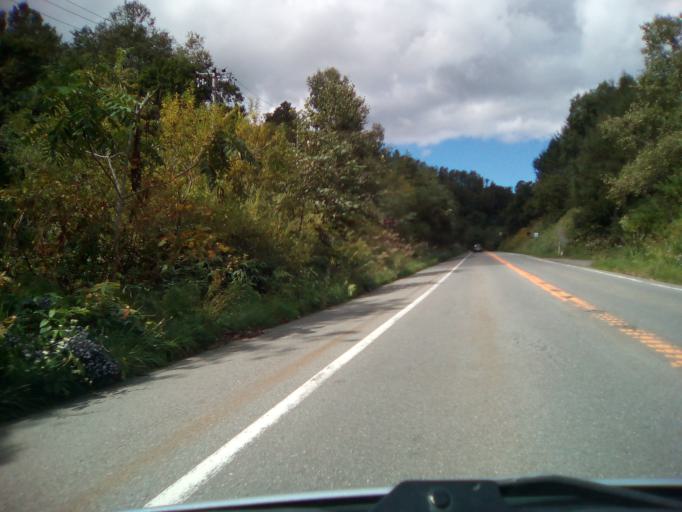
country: JP
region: Hokkaido
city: Date
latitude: 42.5918
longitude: 140.7825
